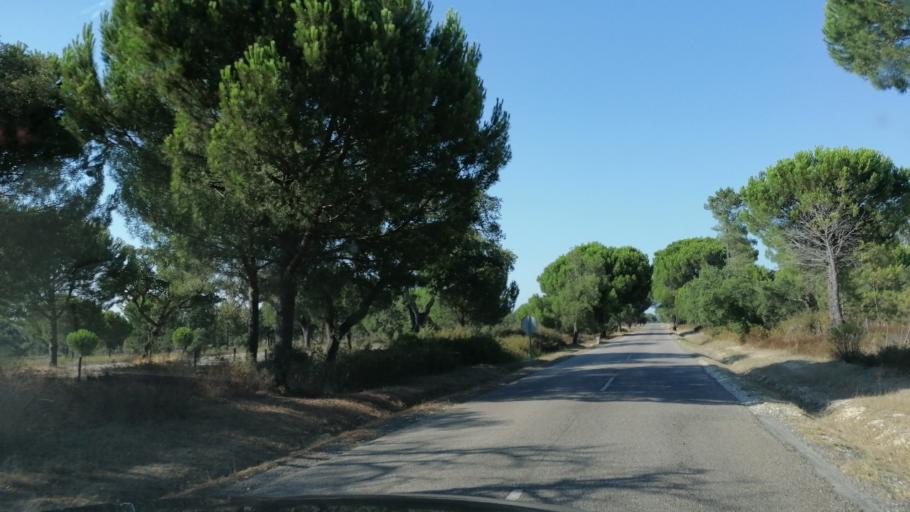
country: PT
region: Santarem
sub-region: Coruche
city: Coruche
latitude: 38.9105
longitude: -8.5262
